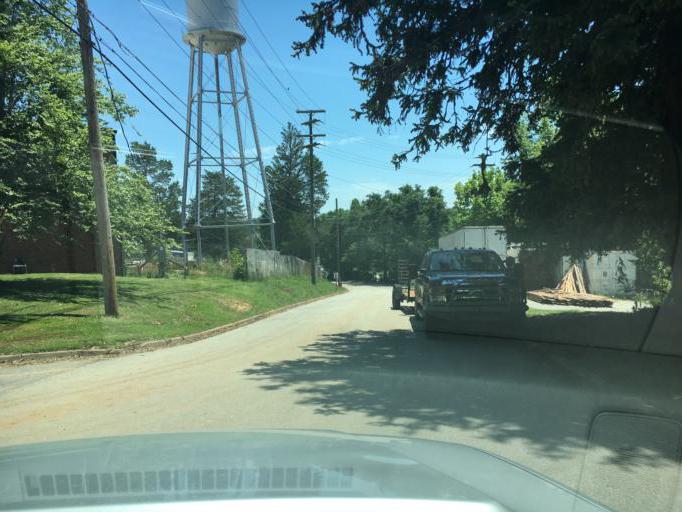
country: US
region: South Carolina
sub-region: Greenville County
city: Greer
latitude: 34.9623
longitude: -82.2097
